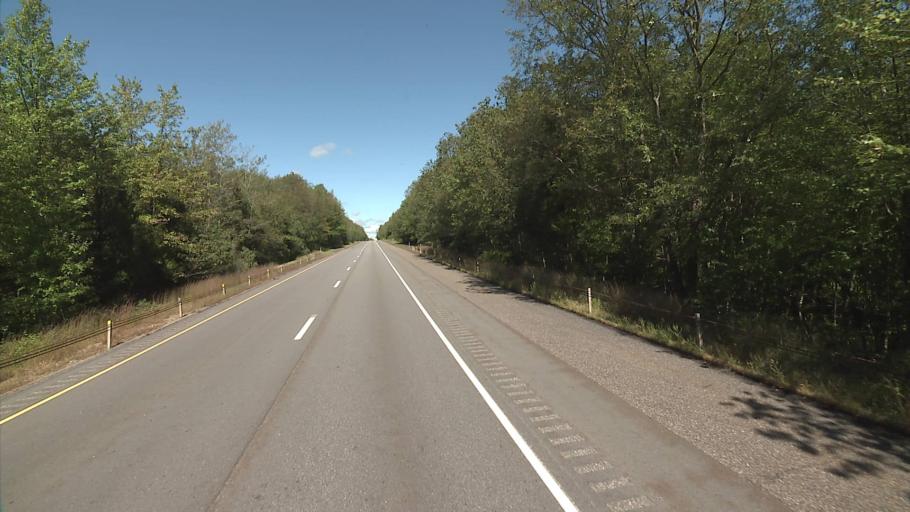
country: US
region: Connecticut
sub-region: New London County
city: Colchester
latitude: 41.5314
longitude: -72.3083
